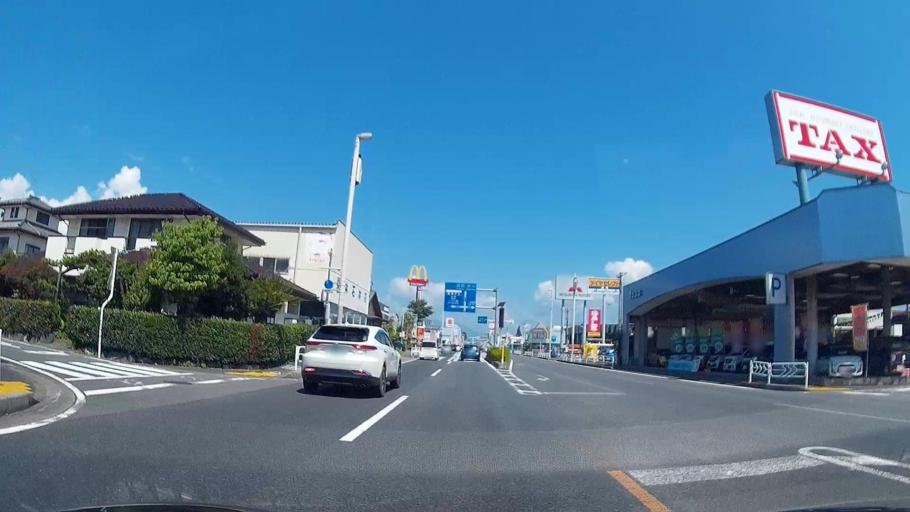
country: JP
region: Gunma
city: Maebashi-shi
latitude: 36.4277
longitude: 139.0554
